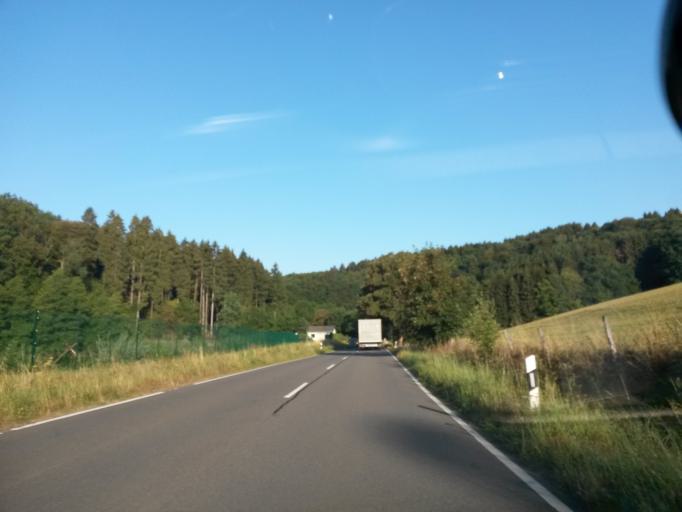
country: DE
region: North Rhine-Westphalia
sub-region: Regierungsbezirk Koln
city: Kurten
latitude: 51.0635
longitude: 7.3082
